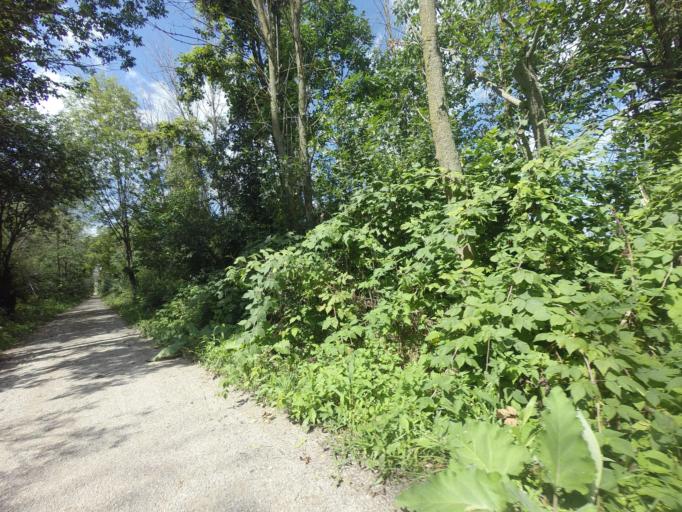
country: CA
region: Ontario
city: Huron East
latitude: 43.6308
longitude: -81.1795
